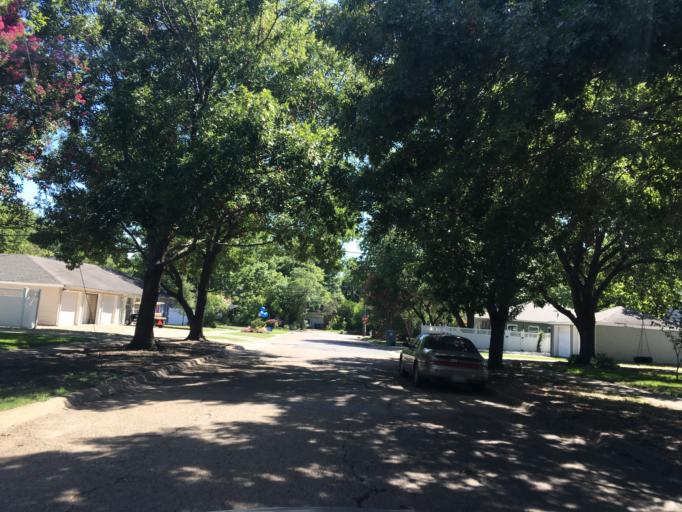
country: US
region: Texas
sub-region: Dallas County
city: Garland
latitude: 32.8412
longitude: -96.6979
